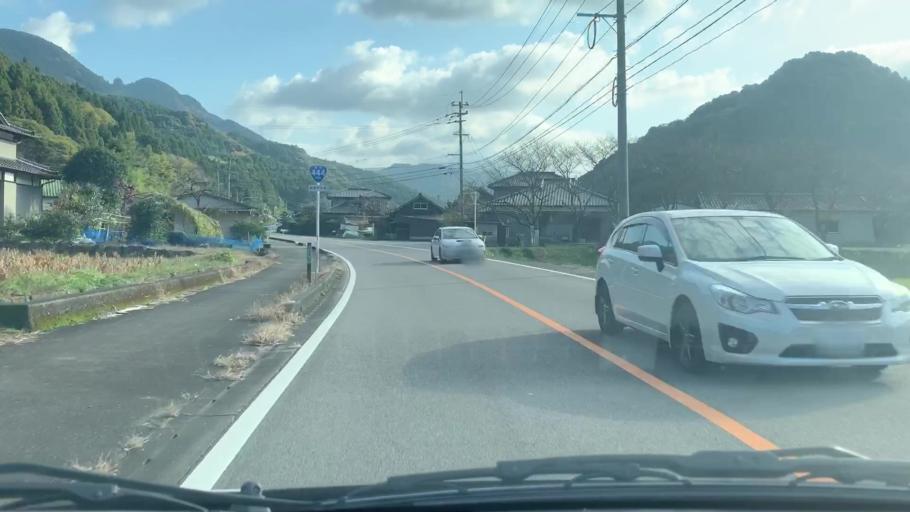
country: JP
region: Saga Prefecture
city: Kashima
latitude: 33.0732
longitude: 130.0683
